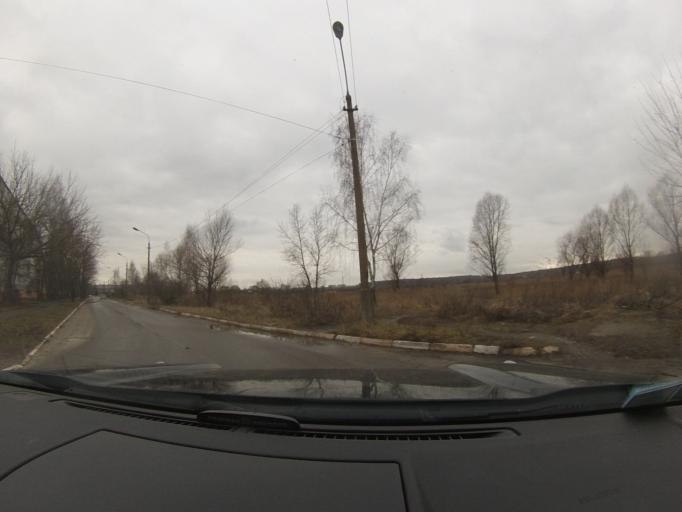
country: RU
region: Moskovskaya
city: Lopatinskiy
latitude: 55.3416
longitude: 38.7127
